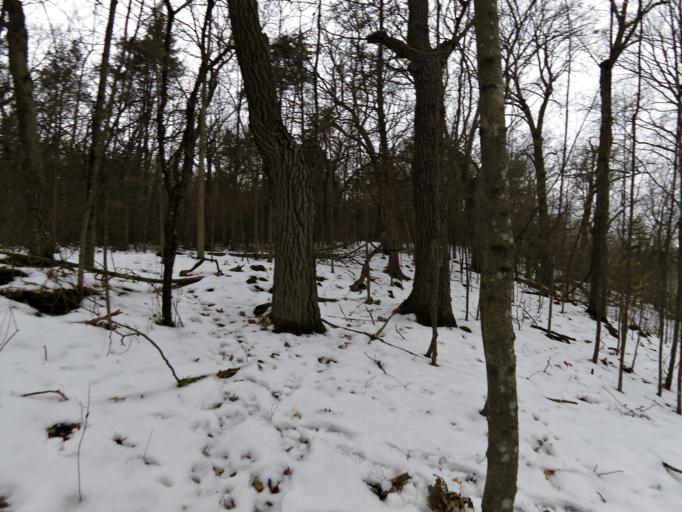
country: US
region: Wisconsin
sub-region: Pierce County
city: Prescott
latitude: 44.8011
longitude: -92.7873
